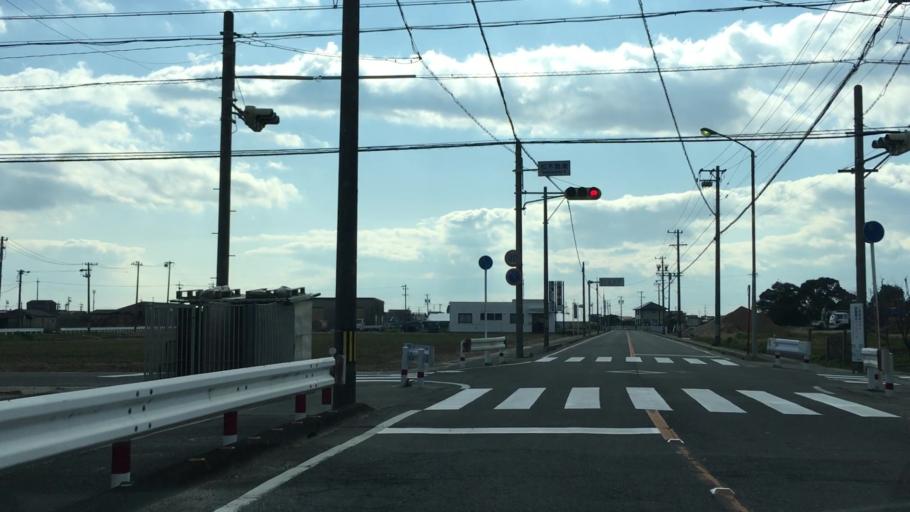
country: JP
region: Aichi
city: Ishiki
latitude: 34.7931
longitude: 137.0403
